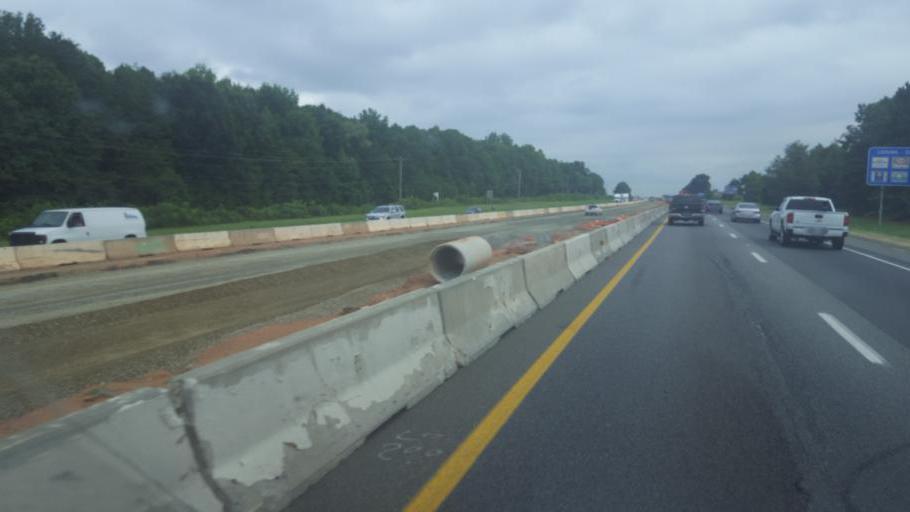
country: US
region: North Carolina
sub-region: Mecklenburg County
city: Cornelius
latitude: 35.4718
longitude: -80.8750
